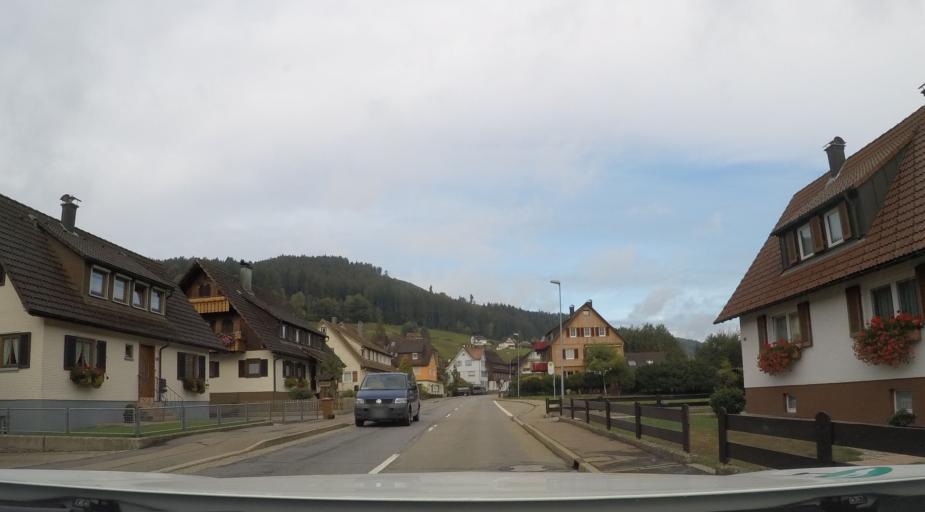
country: DE
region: Baden-Wuerttemberg
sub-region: Karlsruhe Region
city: Baiersbronn
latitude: 48.5239
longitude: 8.3659
